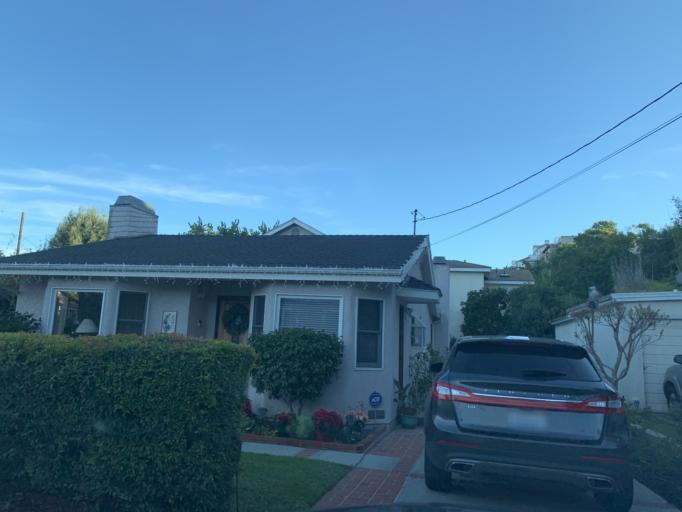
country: US
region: California
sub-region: Los Angeles County
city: Hermosa Beach
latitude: 33.8693
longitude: -118.3996
